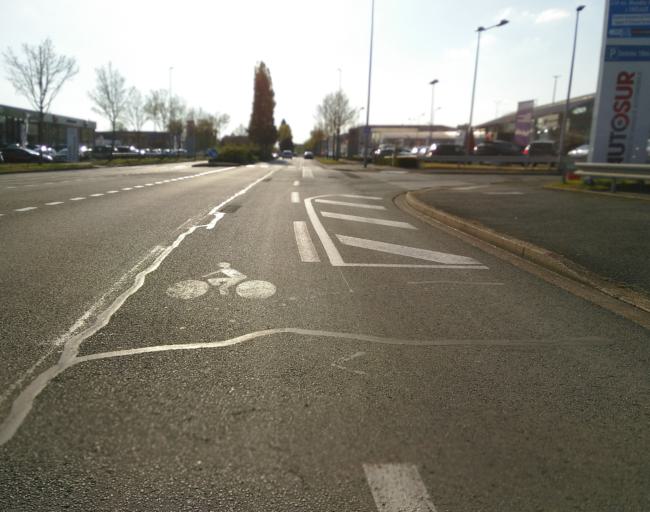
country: FR
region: Pays de la Loire
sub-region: Departement de Maine-et-Loire
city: Angers
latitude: 47.4489
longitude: -0.5334
